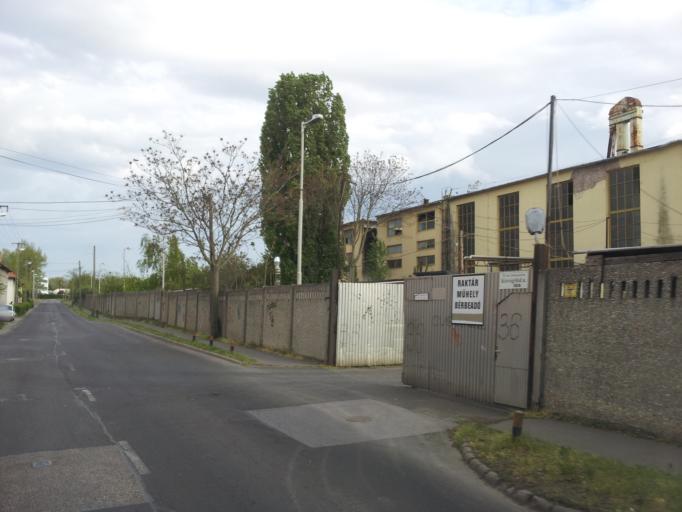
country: HU
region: Budapest
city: Budapest XV. keruelet
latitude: 47.5717
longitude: 19.1263
